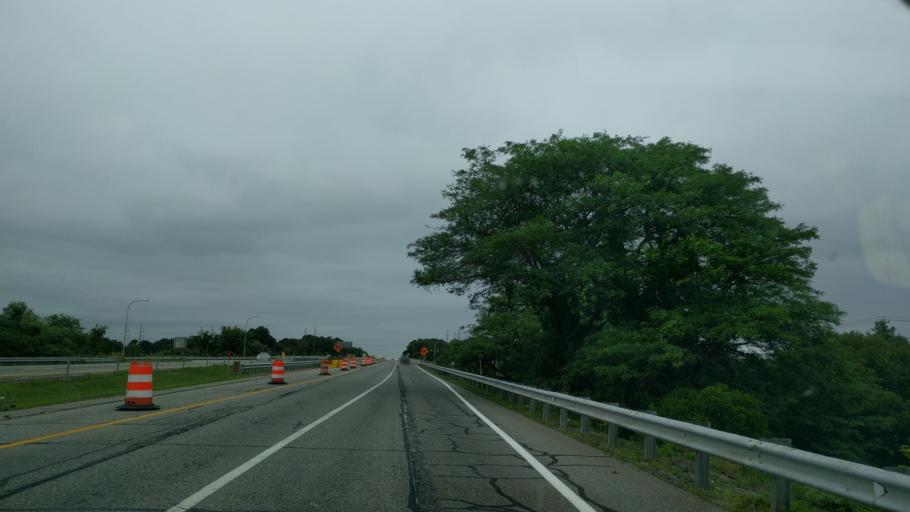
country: US
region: Rhode Island
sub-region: Newport County
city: Portsmouth
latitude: 41.6089
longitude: -71.2547
